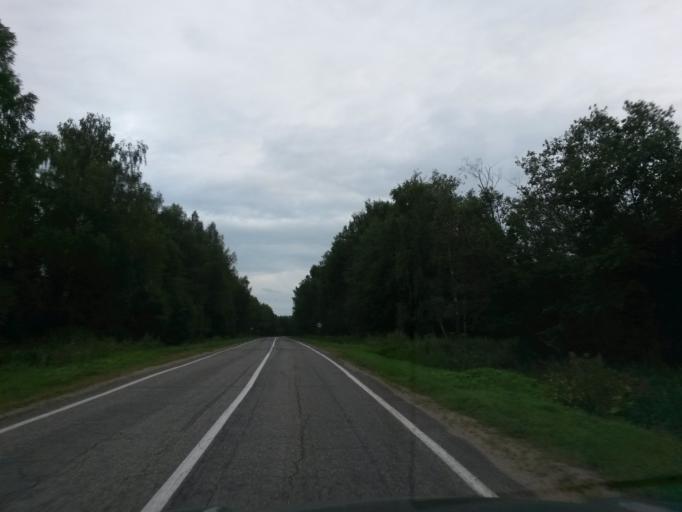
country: RU
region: Jaroslavl
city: Tutayev
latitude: 57.9258
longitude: 39.5066
